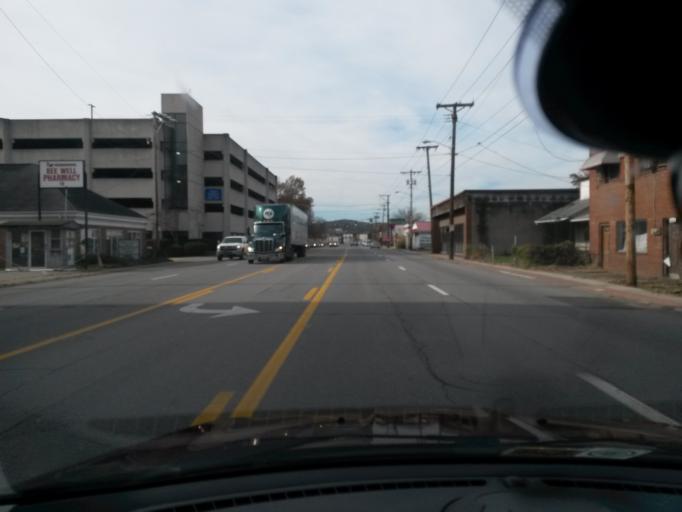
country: US
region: West Virginia
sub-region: Kanawha County
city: Dunbar
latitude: 38.3562
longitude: -81.7249
